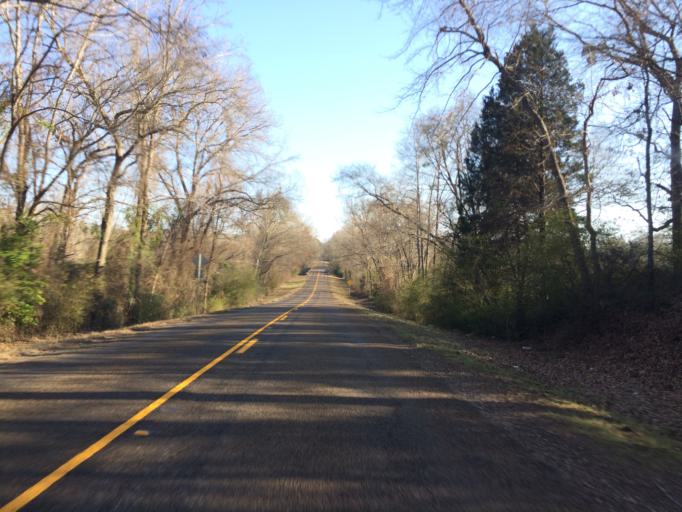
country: US
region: Texas
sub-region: Wood County
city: Quitman
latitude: 32.7128
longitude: -95.3639
